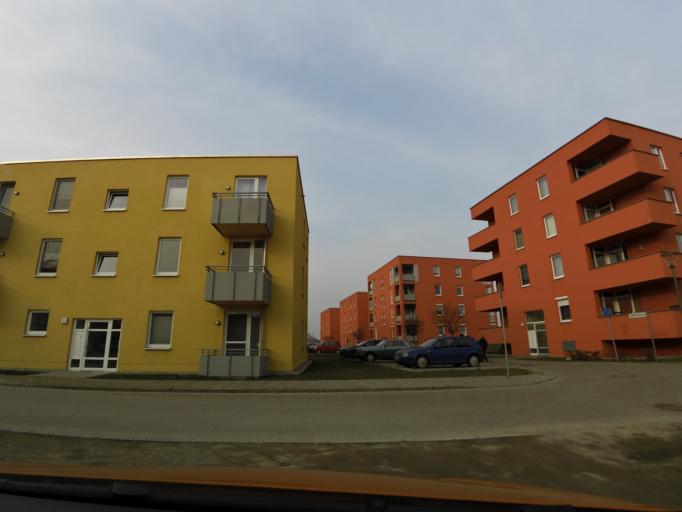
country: DE
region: Brandenburg
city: Frankfurt (Oder)
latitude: 52.3508
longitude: 14.5519
